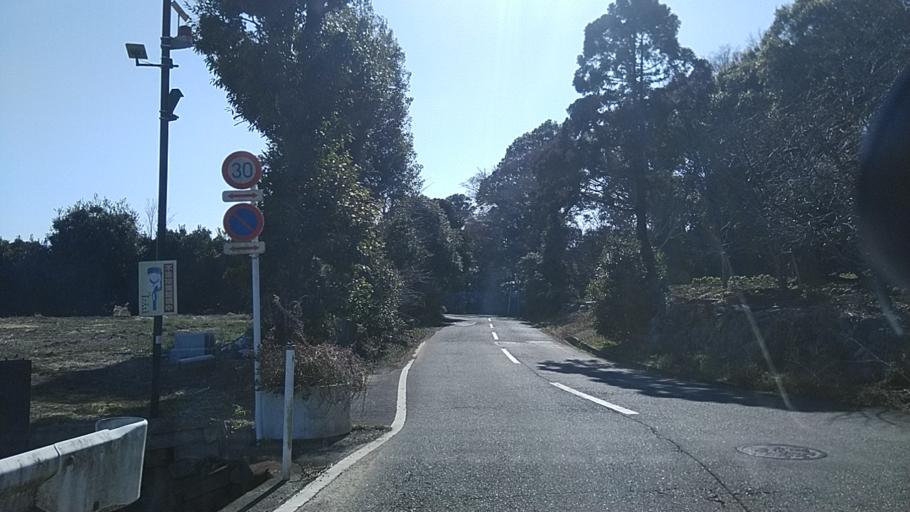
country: JP
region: Kanagawa
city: Fujisawa
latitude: 35.4069
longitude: 139.4739
